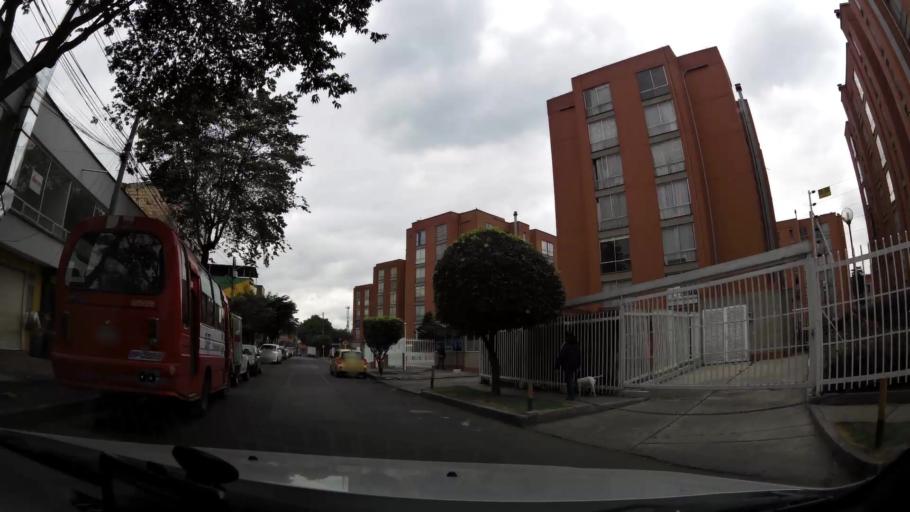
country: CO
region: Bogota D.C.
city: Bogota
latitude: 4.6737
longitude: -74.1222
